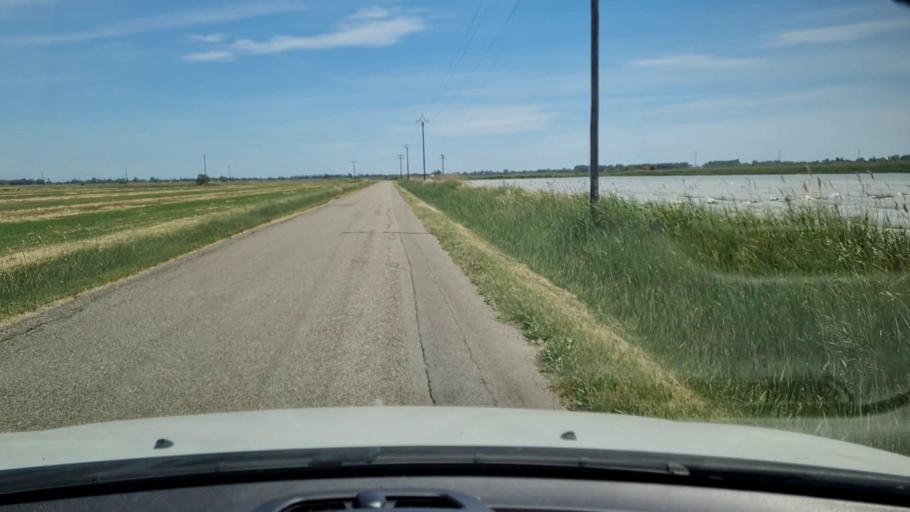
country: FR
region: Languedoc-Roussillon
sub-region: Departement du Gard
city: Saint-Gilles
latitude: 43.6050
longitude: 4.4346
